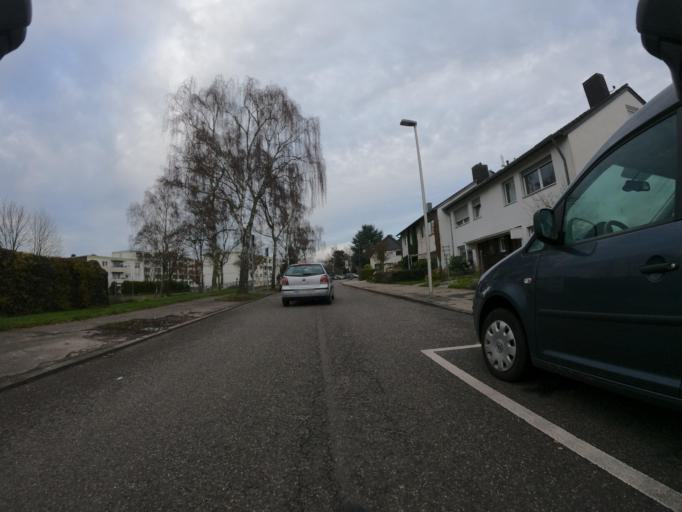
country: DE
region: North Rhine-Westphalia
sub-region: Regierungsbezirk Koln
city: Aachen
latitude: 50.7672
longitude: 6.1157
